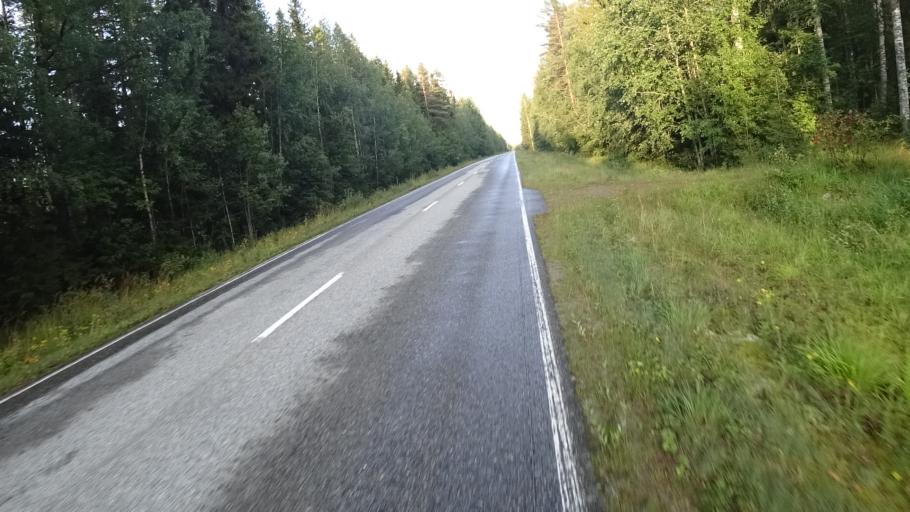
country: FI
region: North Karelia
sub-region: Joensuu
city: Ilomantsi
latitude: 62.6229
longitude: 31.1402
